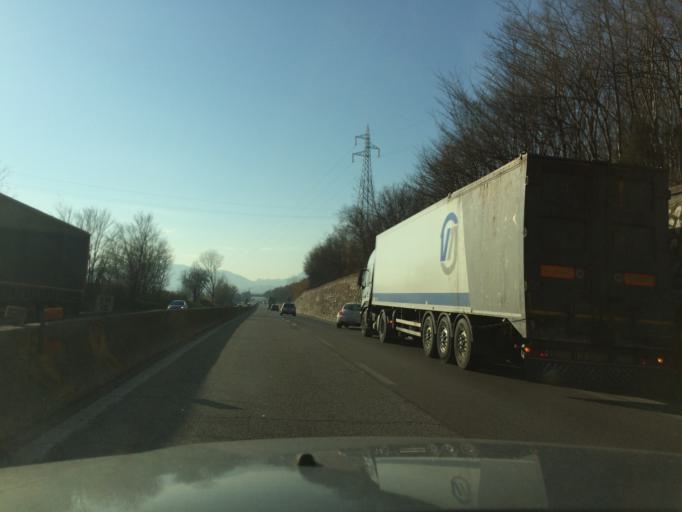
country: IT
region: Umbria
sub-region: Provincia di Terni
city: Narni Scalo
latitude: 42.5649
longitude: 12.5546
